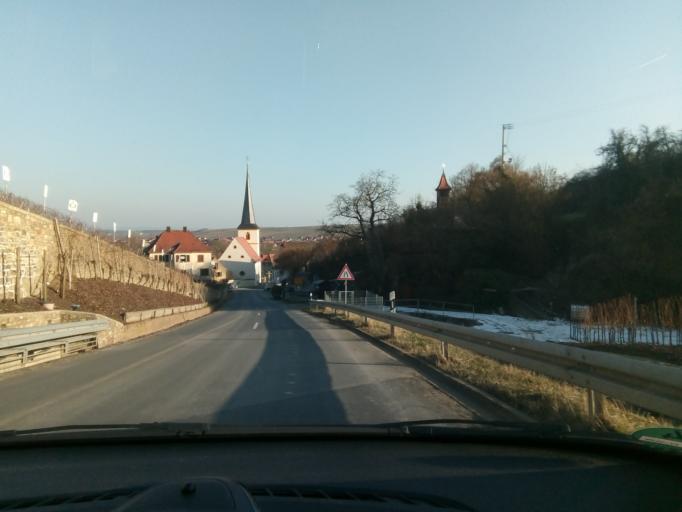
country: DE
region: Bavaria
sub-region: Regierungsbezirk Unterfranken
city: Nordheim
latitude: 49.8633
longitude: 10.1725
